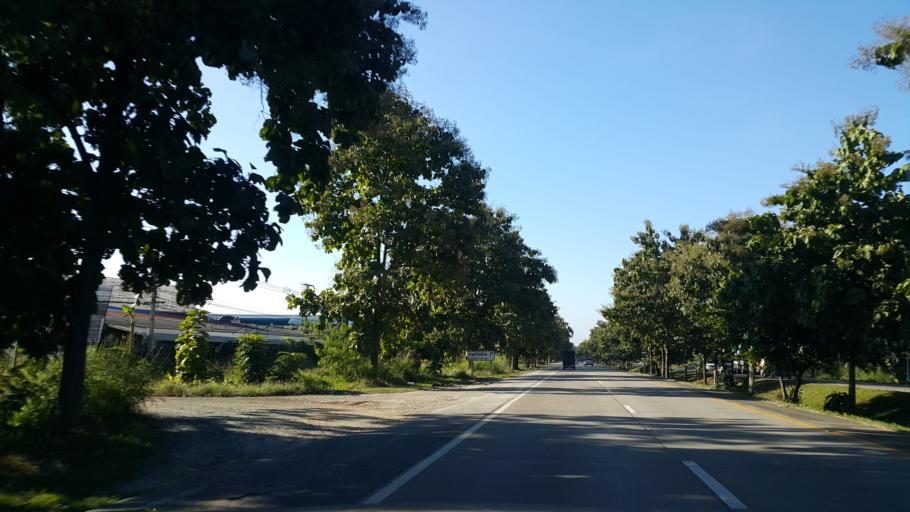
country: TH
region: Lamphun
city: Lamphun
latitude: 18.5310
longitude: 99.0785
